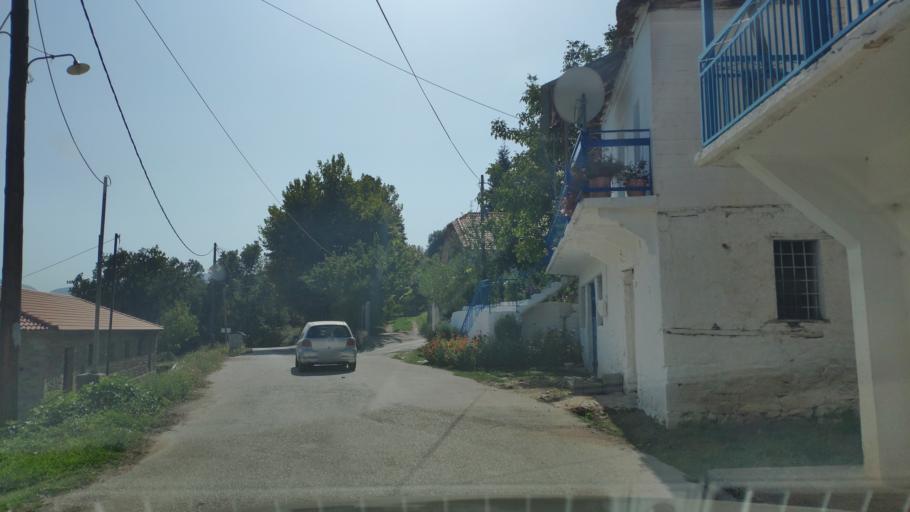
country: GR
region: West Greece
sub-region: Nomos Achaias
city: Aiyira
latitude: 37.9492
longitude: 22.3249
